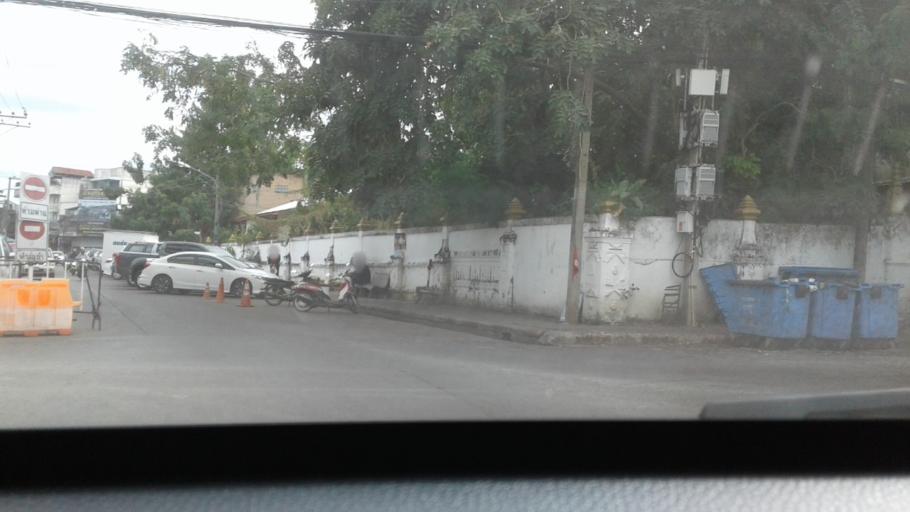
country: TH
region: Changwat Udon Thani
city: Udon Thani
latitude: 17.4166
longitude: 102.7903
